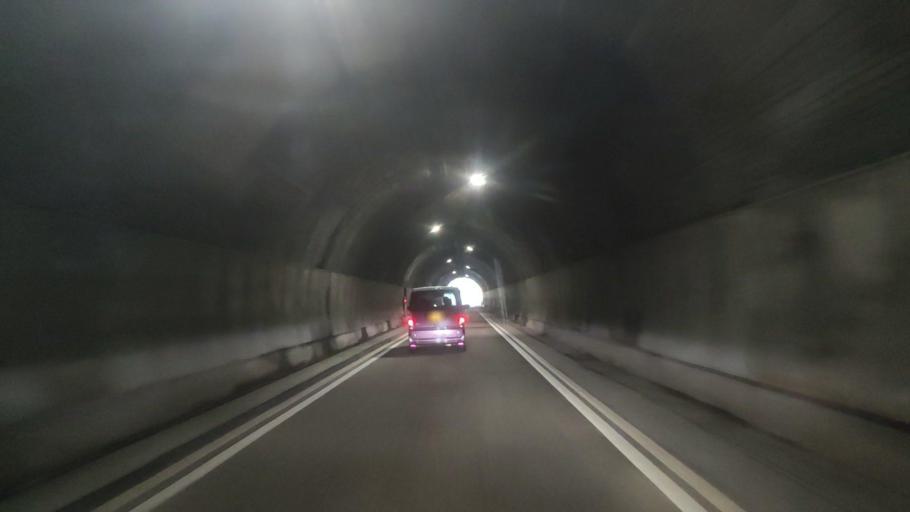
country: JP
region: Fukui
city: Takefu
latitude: 35.8465
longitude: 136.1249
